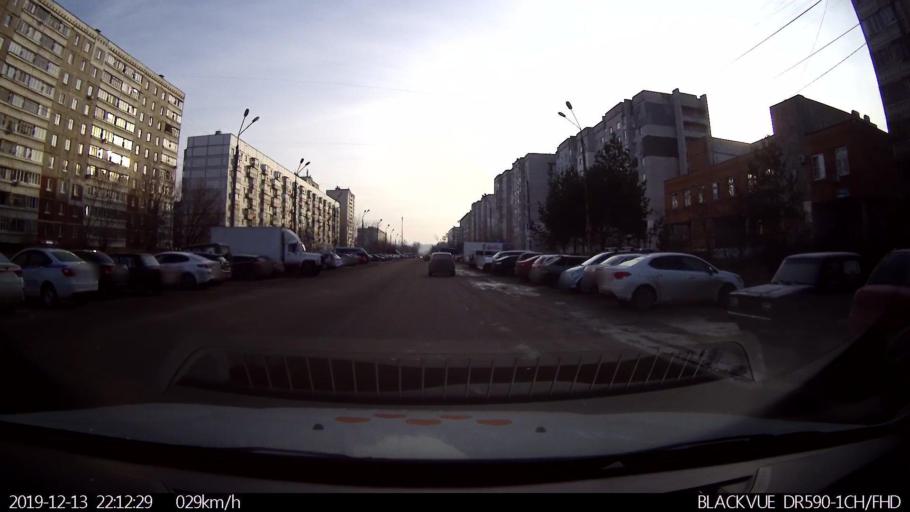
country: RU
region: Nizjnij Novgorod
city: Nizhniy Novgorod
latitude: 56.2740
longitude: 43.8826
